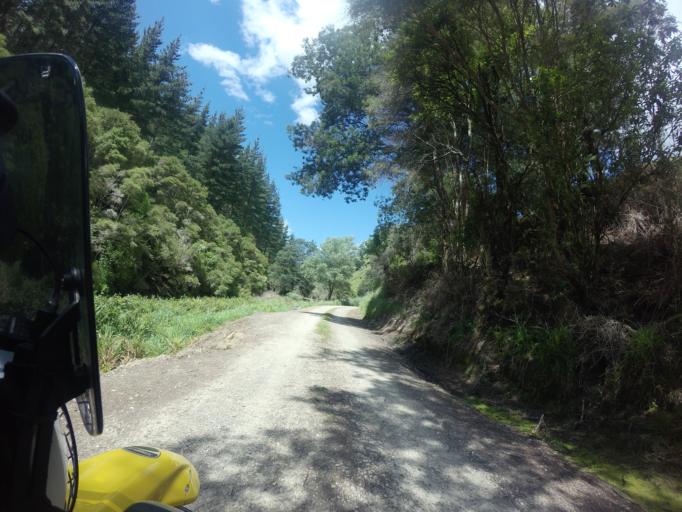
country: NZ
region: Hawke's Bay
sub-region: Wairoa District
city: Wairoa
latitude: -38.9705
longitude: 177.6707
